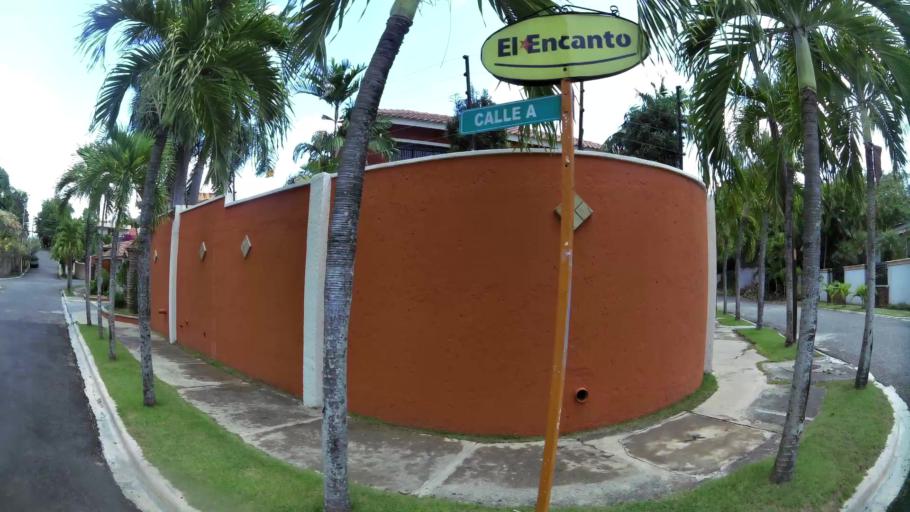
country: DO
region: Santiago
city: Santiago de los Caballeros
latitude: 19.4687
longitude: -70.6773
